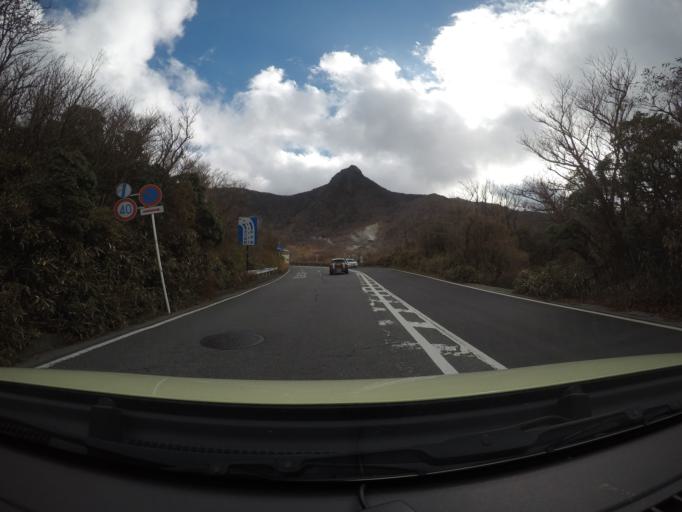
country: JP
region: Kanagawa
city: Hakone
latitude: 35.2435
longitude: 139.0179
